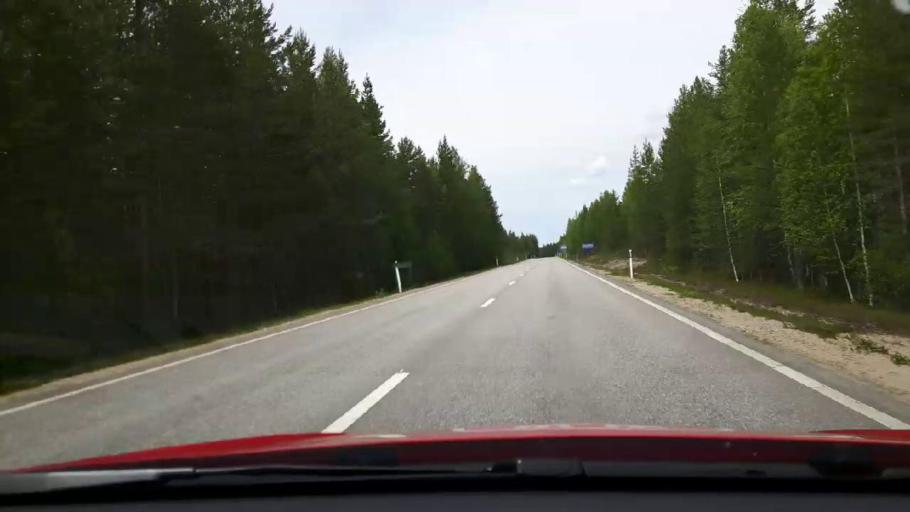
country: SE
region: Jaemtland
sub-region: Harjedalens Kommun
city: Sveg
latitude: 62.1151
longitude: 14.1774
